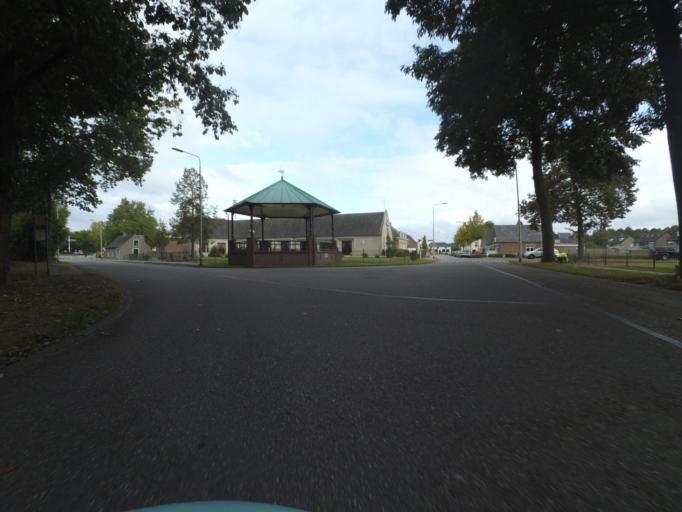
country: NL
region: Utrecht
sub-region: Gemeente Utrechtse Heuvelrug
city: Amerongen
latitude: 51.9684
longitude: 5.4553
